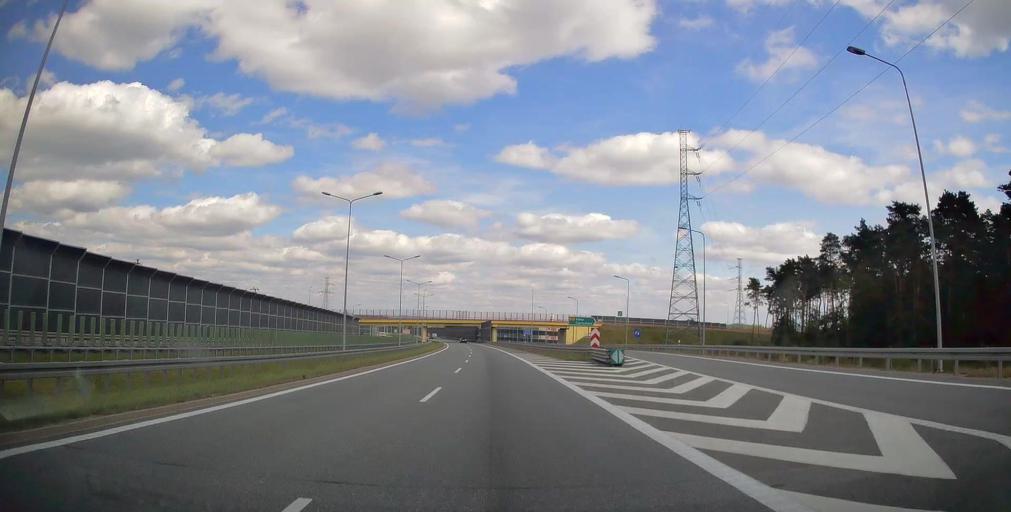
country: PL
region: Swietokrzyskie
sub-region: Powiat kielecki
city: Piekoszow
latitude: 50.8555
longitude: 20.5046
